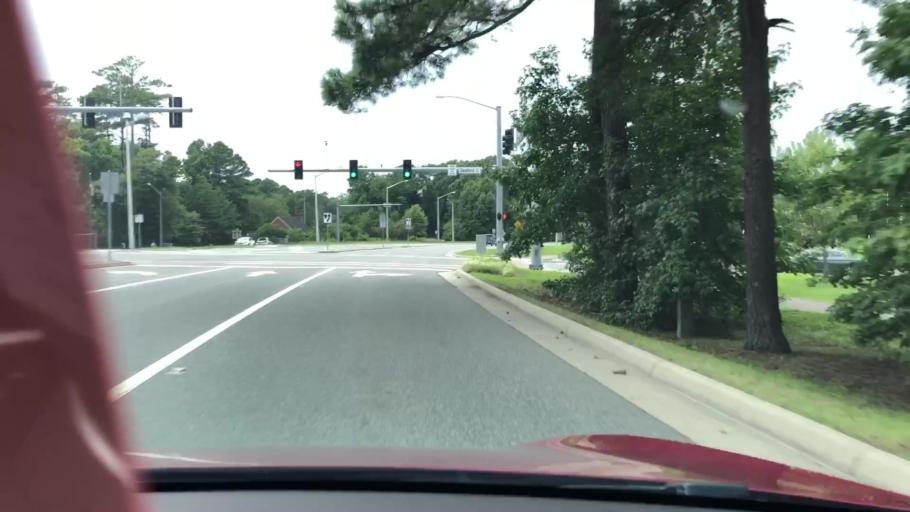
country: US
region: Virginia
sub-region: City of Virginia Beach
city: Virginia Beach
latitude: 36.8110
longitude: -75.9919
